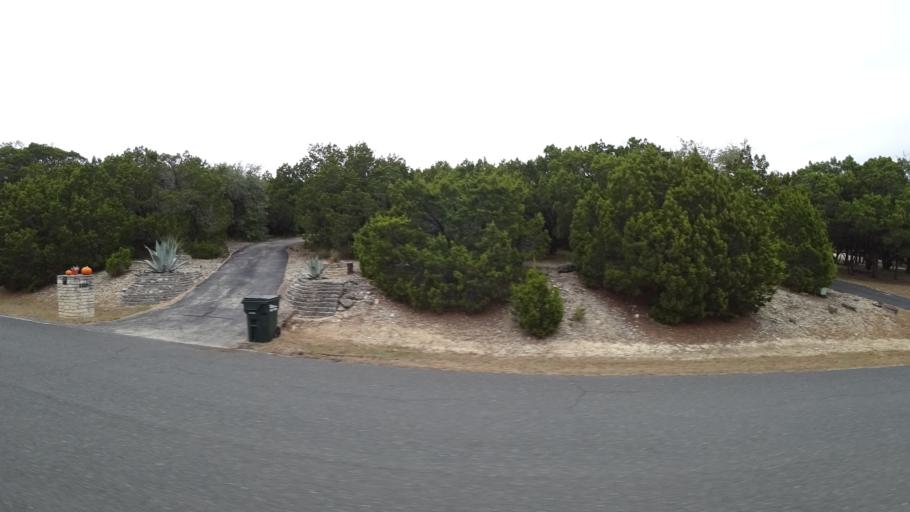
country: US
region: Texas
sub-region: Travis County
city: West Lake Hills
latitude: 30.3721
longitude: -97.8132
